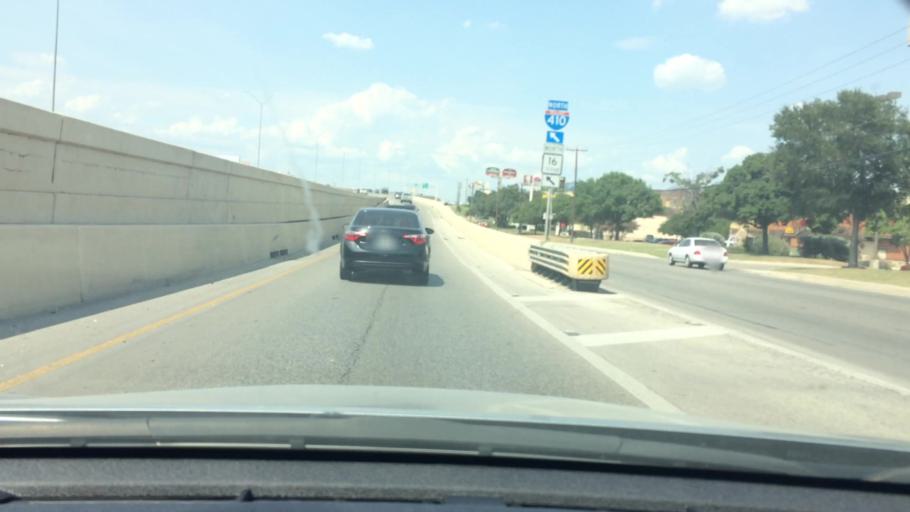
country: US
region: Texas
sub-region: Bexar County
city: Leon Valley
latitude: 29.4609
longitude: -98.6225
